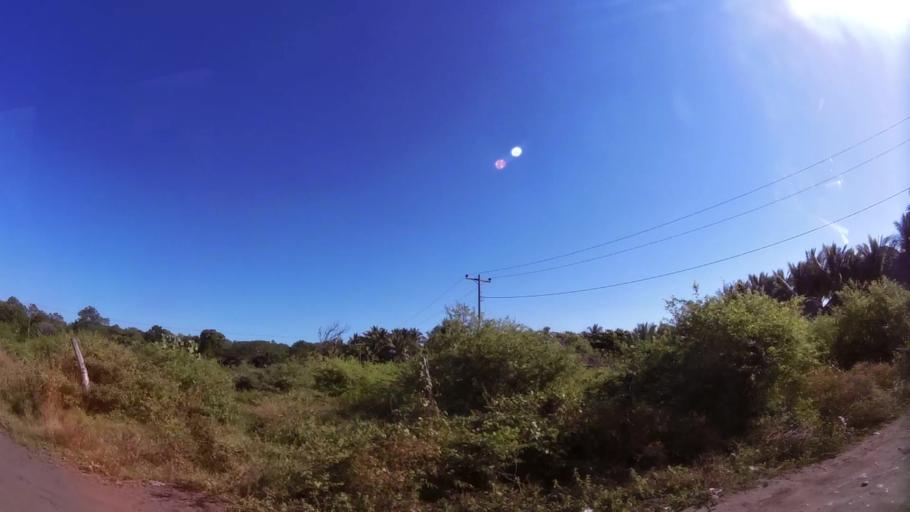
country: GT
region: Santa Rosa
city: Guazacapan
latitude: 13.8569
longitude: -90.3901
